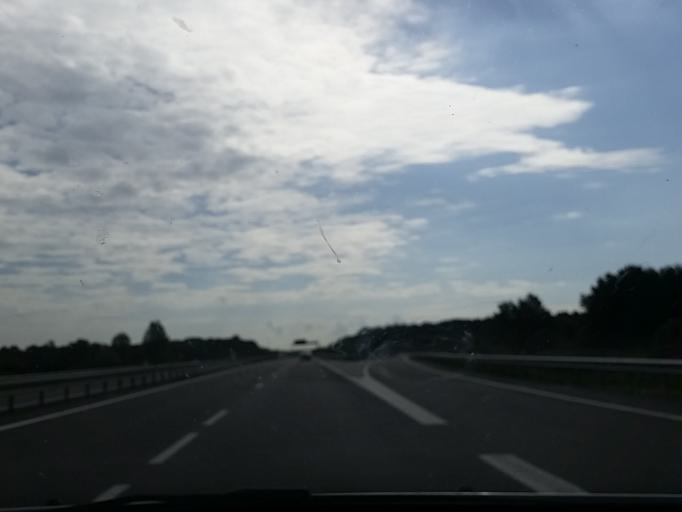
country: FR
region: Centre
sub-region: Departement du Loir-et-Cher
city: Chatres-sur-Cher
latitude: 47.2949
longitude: 1.9184
